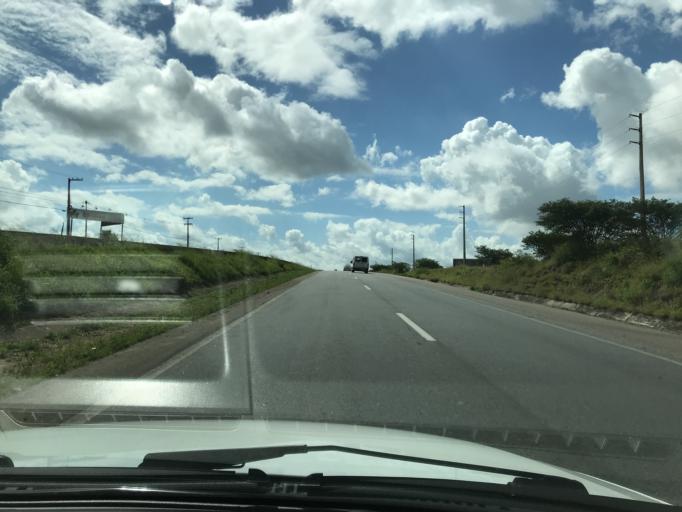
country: BR
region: Pernambuco
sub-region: Gravata
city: Gravata
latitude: -8.2071
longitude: -35.6057
